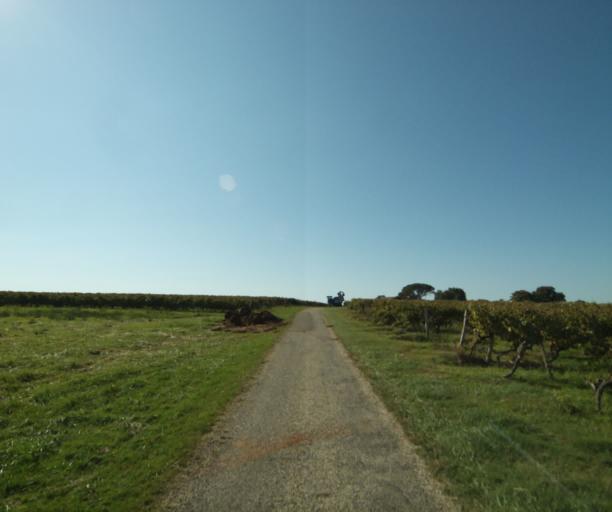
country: FR
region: Aquitaine
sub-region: Departement des Landes
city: Gabarret
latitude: 43.9508
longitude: -0.0060
